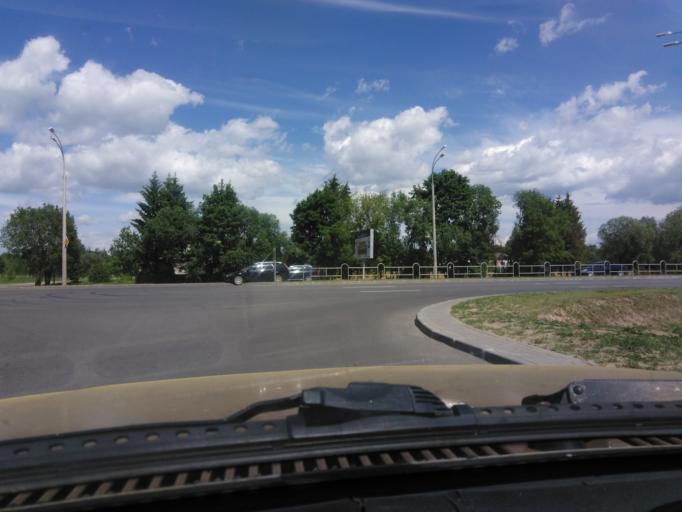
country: BY
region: Mogilev
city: Buynichy
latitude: 53.9321
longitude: 30.2590
